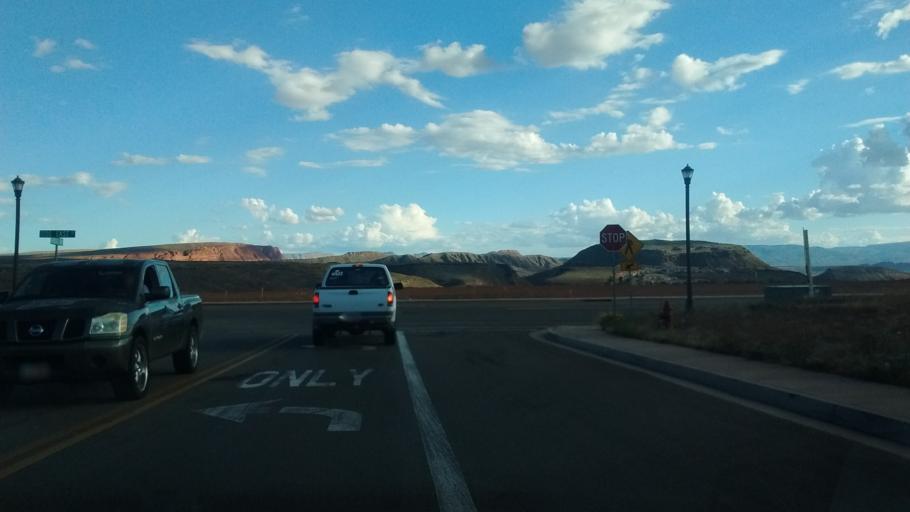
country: US
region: Utah
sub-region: Washington County
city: Washington
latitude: 37.1446
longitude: -113.4878
